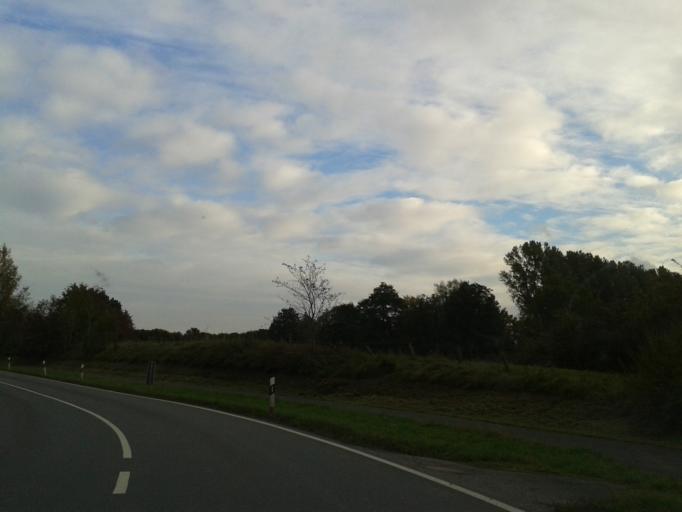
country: DE
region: North Rhine-Westphalia
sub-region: Regierungsbezirk Detmold
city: Horn
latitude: 51.8724
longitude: 8.9558
